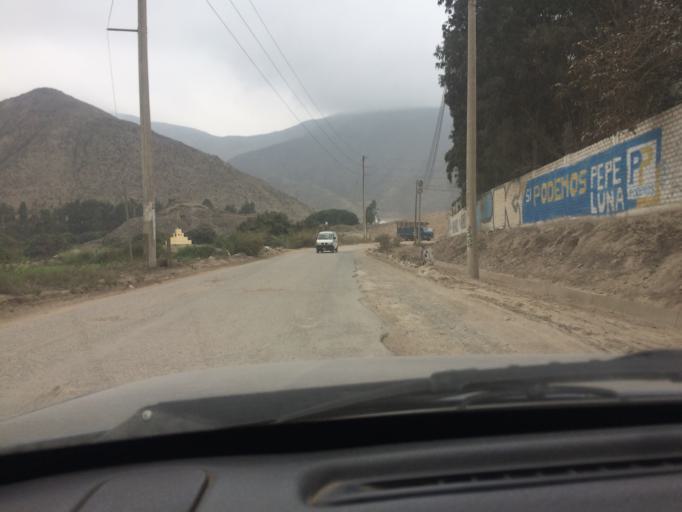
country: PE
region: Lima
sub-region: Lima
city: Cieneguilla
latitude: -12.1775
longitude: -76.8634
